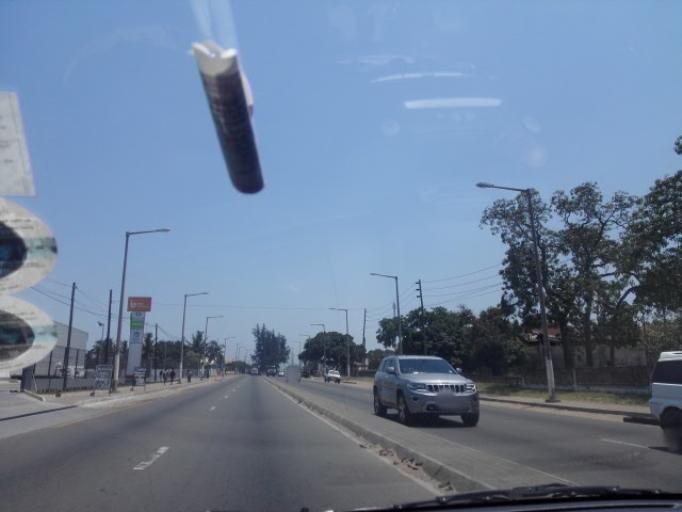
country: MZ
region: Maputo City
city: Maputo
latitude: -25.9004
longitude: 32.5644
